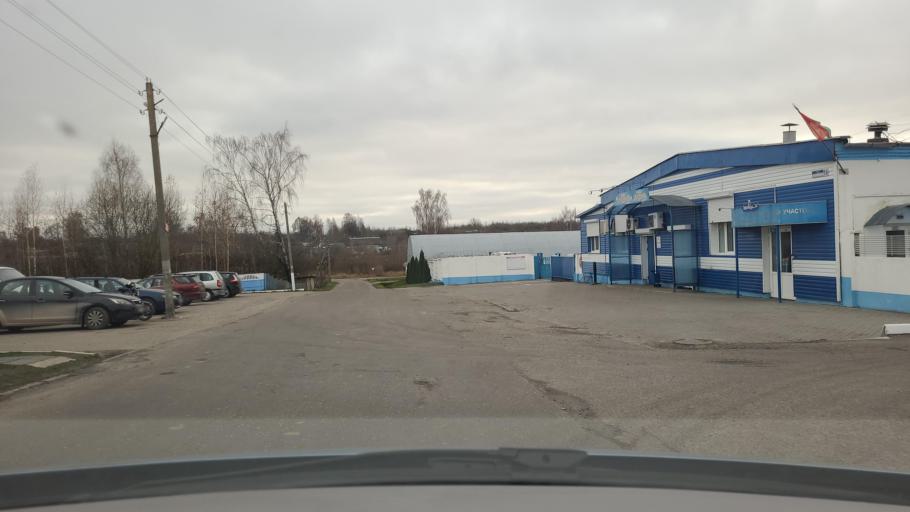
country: BY
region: Minsk
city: Khalopyenichy
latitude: 54.5146
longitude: 28.9549
